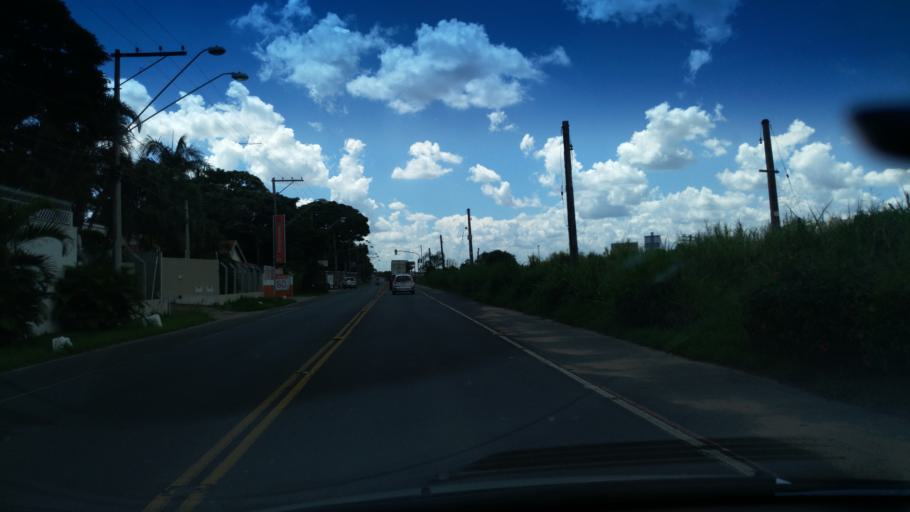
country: BR
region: Sao Paulo
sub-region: Valinhos
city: Valinhos
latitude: -22.9933
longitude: -46.9900
